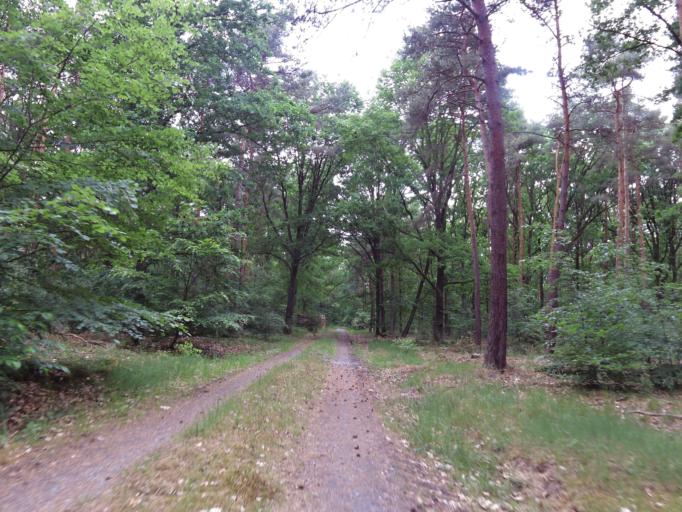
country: DE
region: Hesse
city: Morfelden-Walldorf
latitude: 50.0308
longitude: 8.5990
